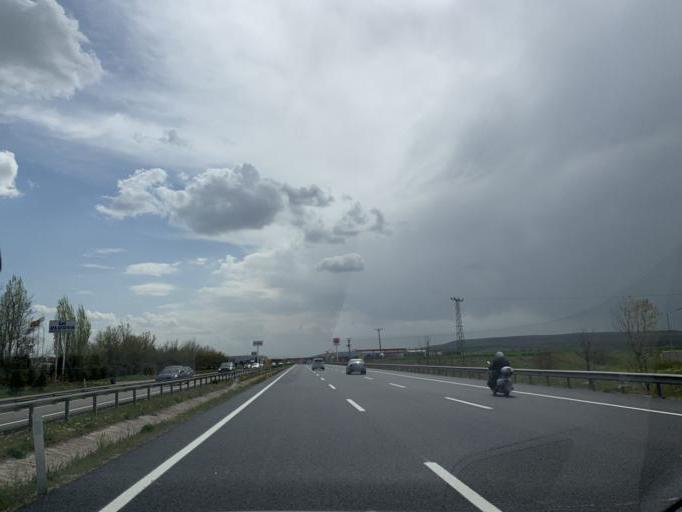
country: TR
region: Ankara
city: Polatli
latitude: 39.6587
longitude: 32.2205
